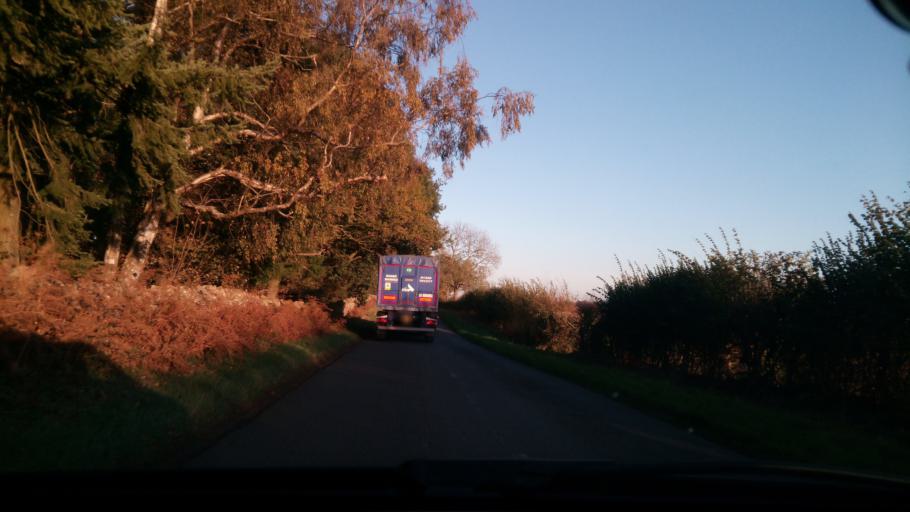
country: GB
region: England
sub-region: Peterborough
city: Wittering
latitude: 52.6260
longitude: -0.4390
